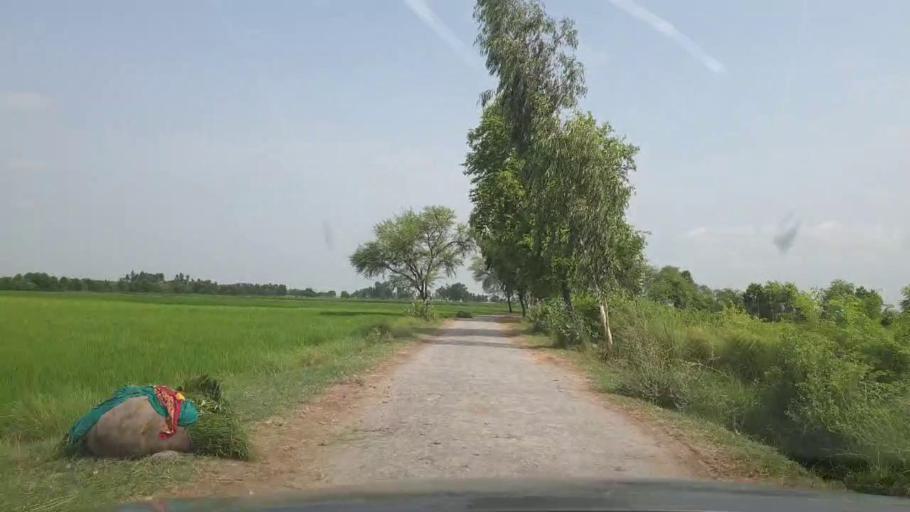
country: PK
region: Sindh
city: Ratodero
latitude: 27.8515
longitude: 68.2998
